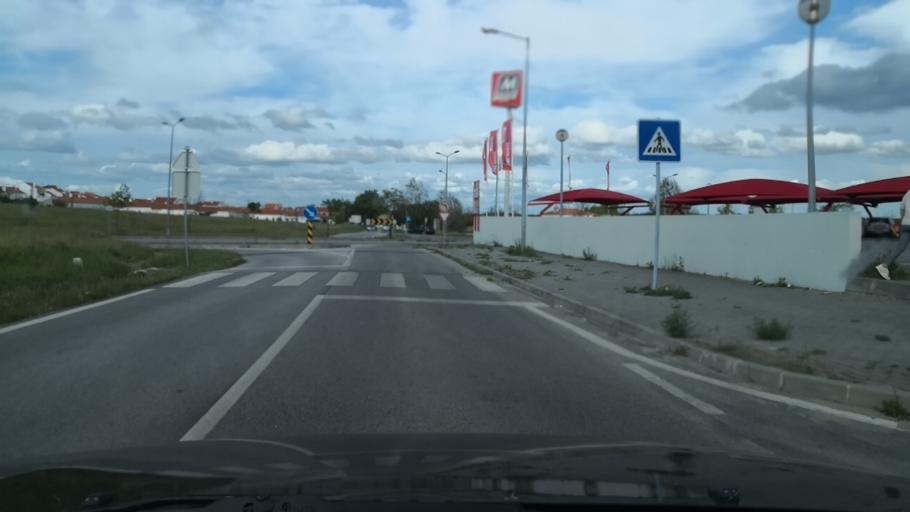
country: PT
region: Evora
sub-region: Evora
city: Evora
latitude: 38.5813
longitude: -7.9032
